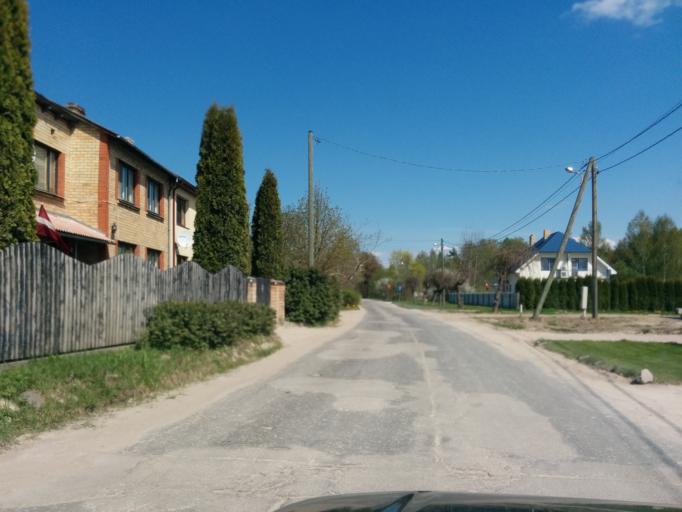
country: LV
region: Jelgava
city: Jelgava
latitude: 56.6285
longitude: 23.7322
